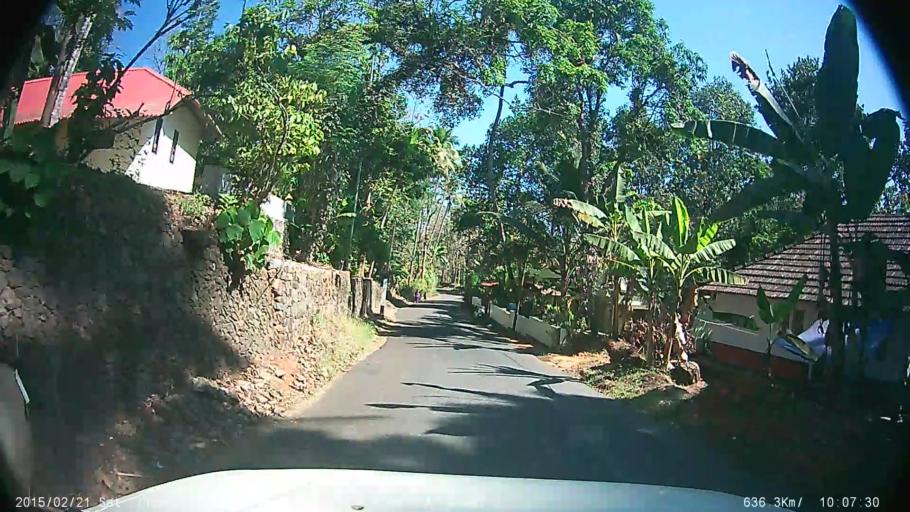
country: IN
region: Kerala
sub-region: Ernakulam
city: Piravam
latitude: 9.8727
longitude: 76.6064
